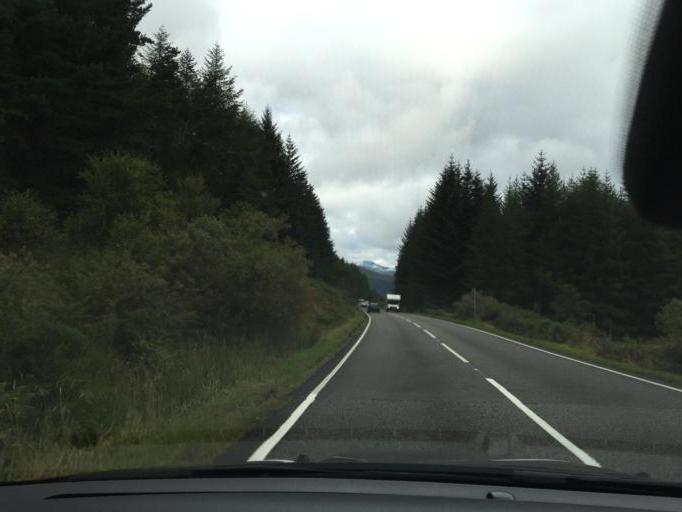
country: GB
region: Scotland
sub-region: Argyll and Bute
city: Garelochhead
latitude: 56.4813
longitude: -4.7355
